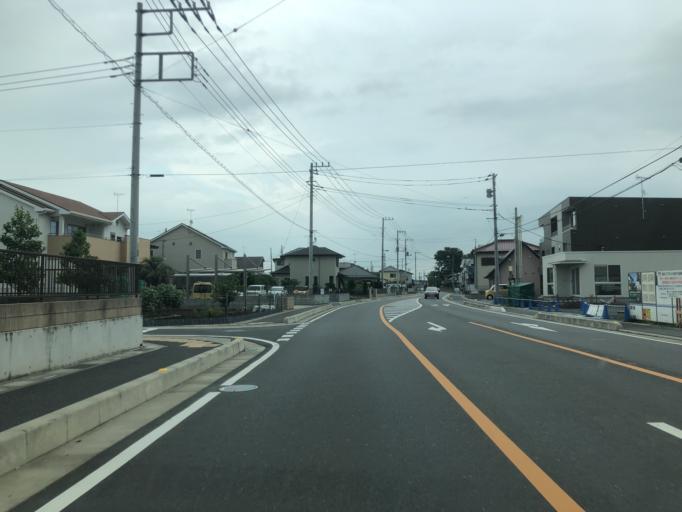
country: JP
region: Saitama
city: Sakado
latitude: 36.0011
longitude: 139.4000
